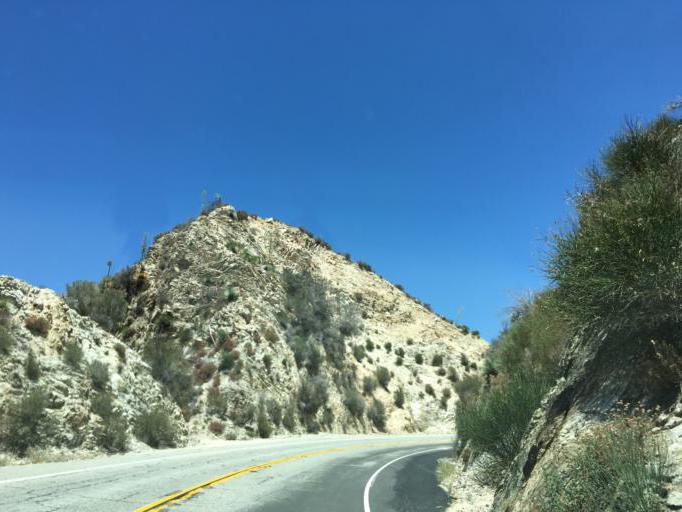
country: US
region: California
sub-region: Los Angeles County
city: La Crescenta-Montrose
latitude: 34.2979
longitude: -118.1660
